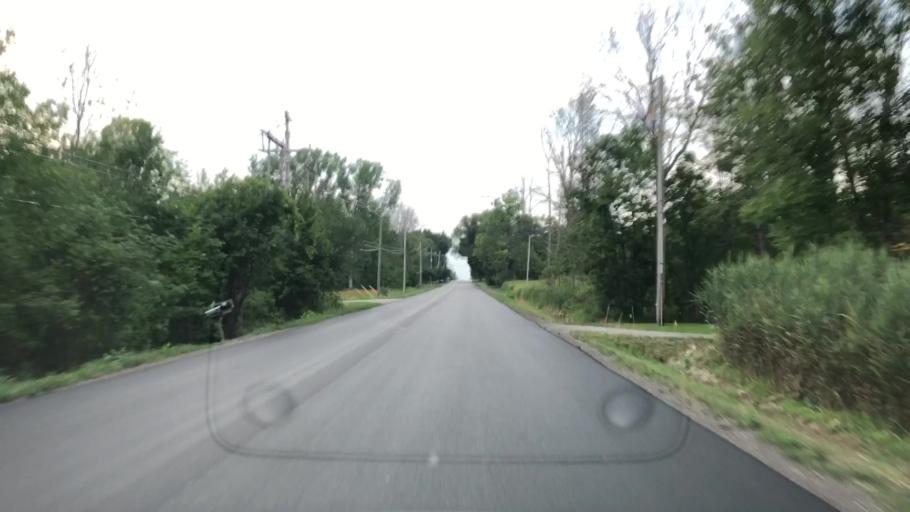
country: US
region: New York
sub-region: Erie County
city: Billington Heights
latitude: 42.8120
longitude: -78.6059
